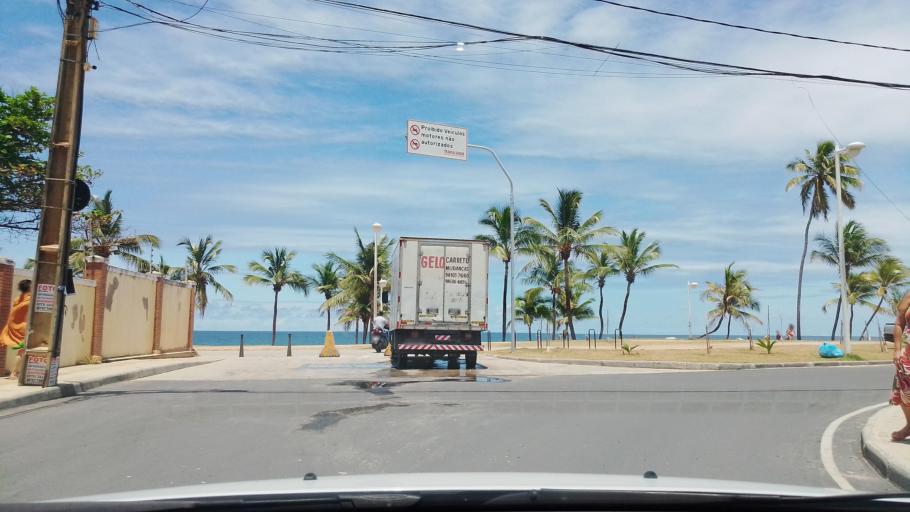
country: BR
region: Bahia
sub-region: Lauro De Freitas
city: Lauro de Freitas
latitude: -12.9386
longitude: -38.3297
